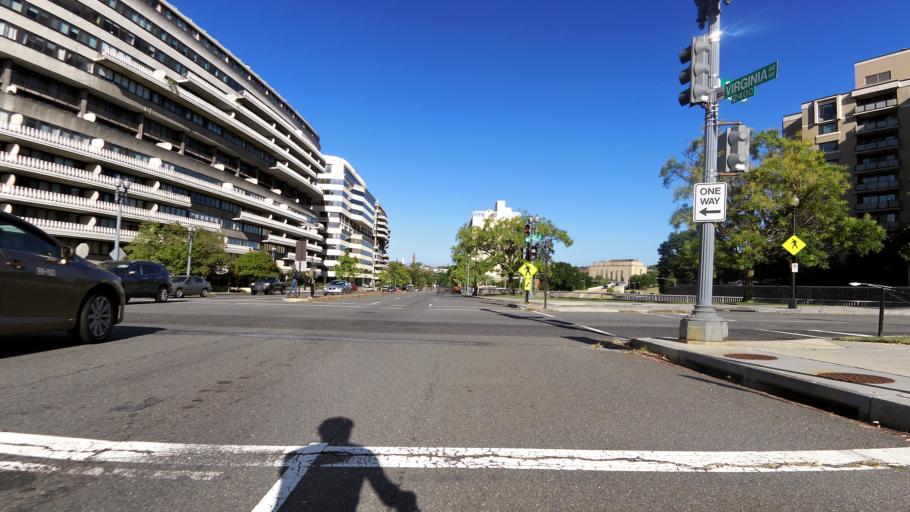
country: US
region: Washington, D.C.
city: Washington, D.C.
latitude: 38.8991
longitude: -77.0536
